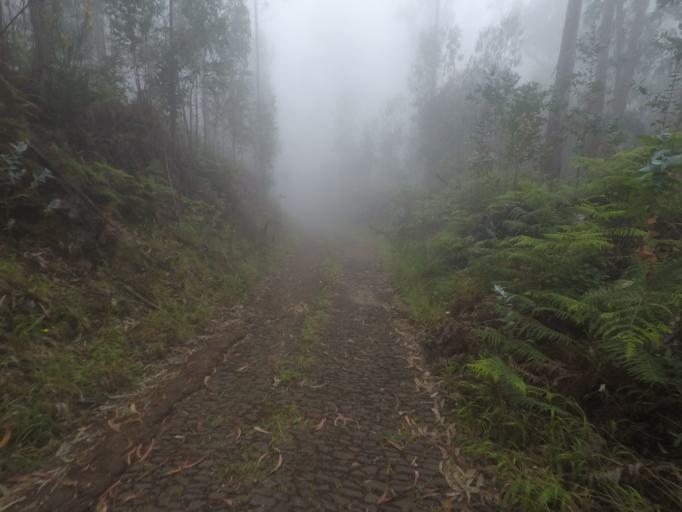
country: PT
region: Madeira
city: Ponta do Sol
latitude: 32.7177
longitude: -17.0934
